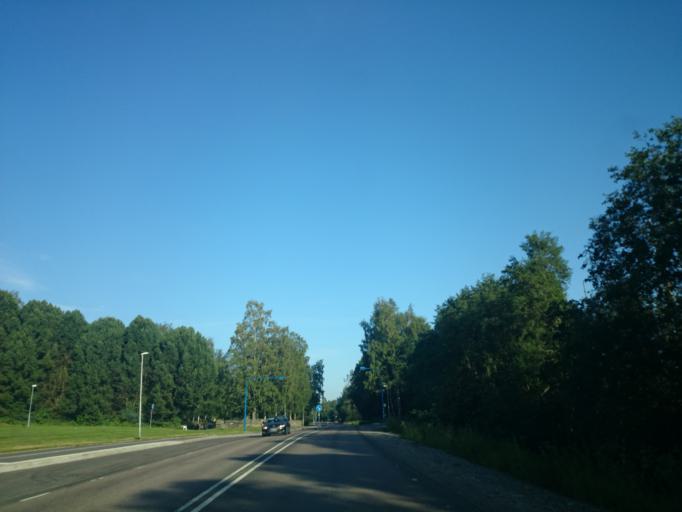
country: SE
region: Vaesternorrland
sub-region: Sundsvalls Kommun
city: Sundsvall
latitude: 62.3970
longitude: 17.2674
